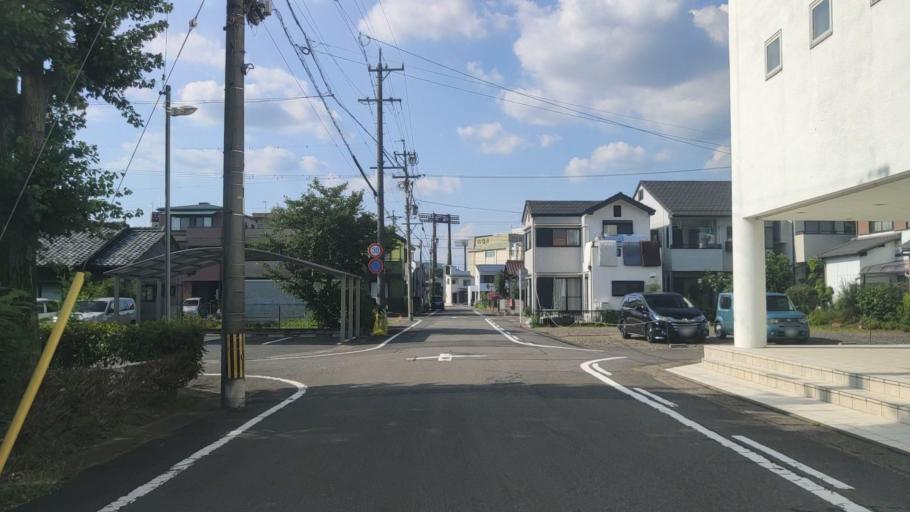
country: JP
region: Gifu
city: Gifu-shi
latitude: 35.4368
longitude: 136.7641
